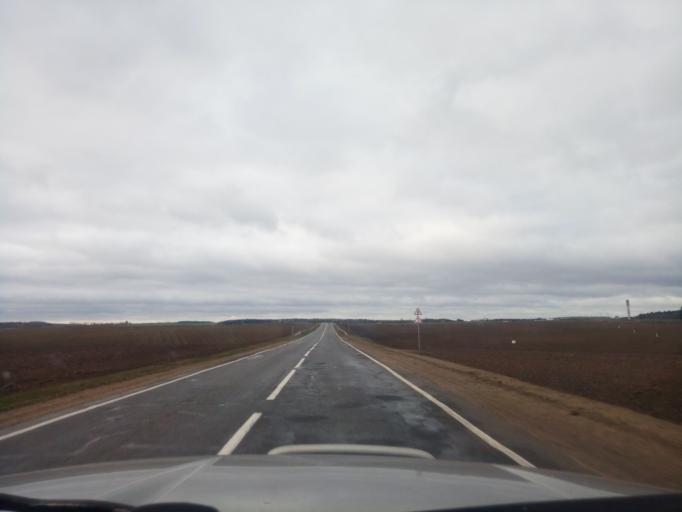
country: BY
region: Minsk
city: Kapyl'
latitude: 53.1996
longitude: 27.2091
